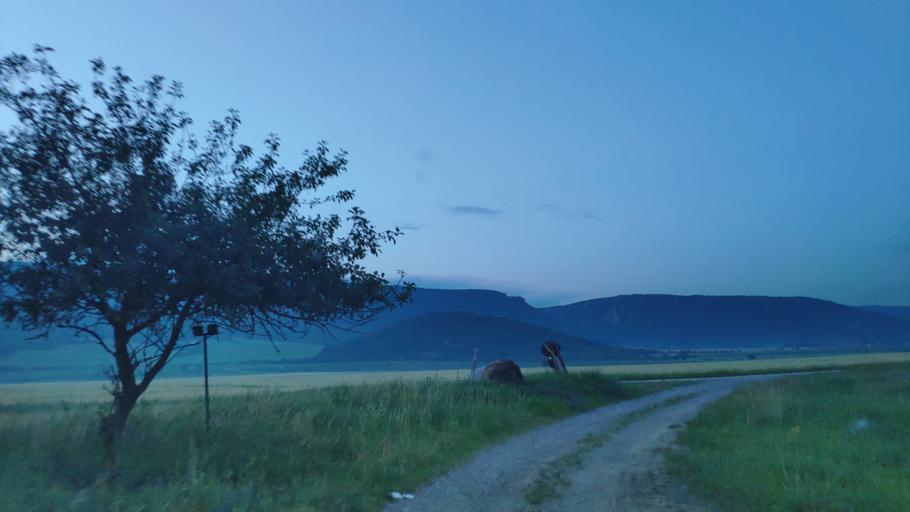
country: SK
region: Kosicky
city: Medzev
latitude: 48.5880
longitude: 20.8018
